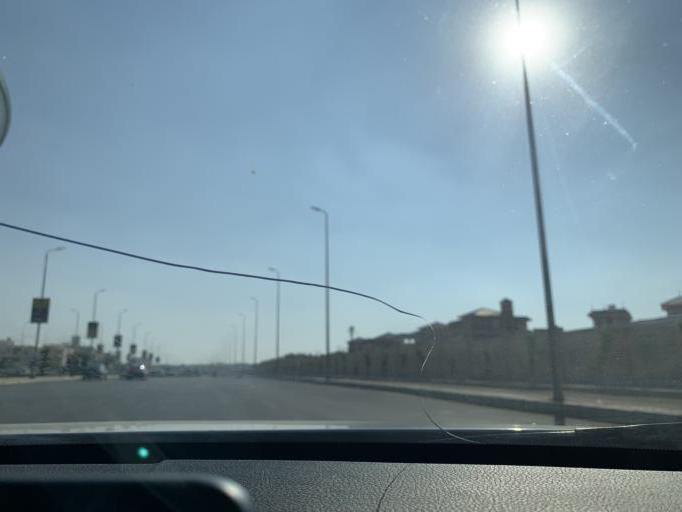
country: EG
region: Muhafazat al Qalyubiyah
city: Al Khankah
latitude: 30.0185
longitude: 31.4747
